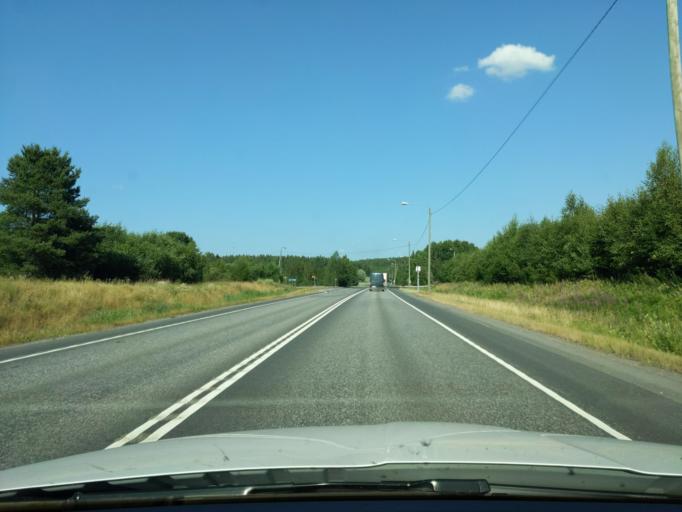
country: FI
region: Paijanne Tavastia
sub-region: Lahti
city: Hollola
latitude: 60.9487
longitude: 25.4213
